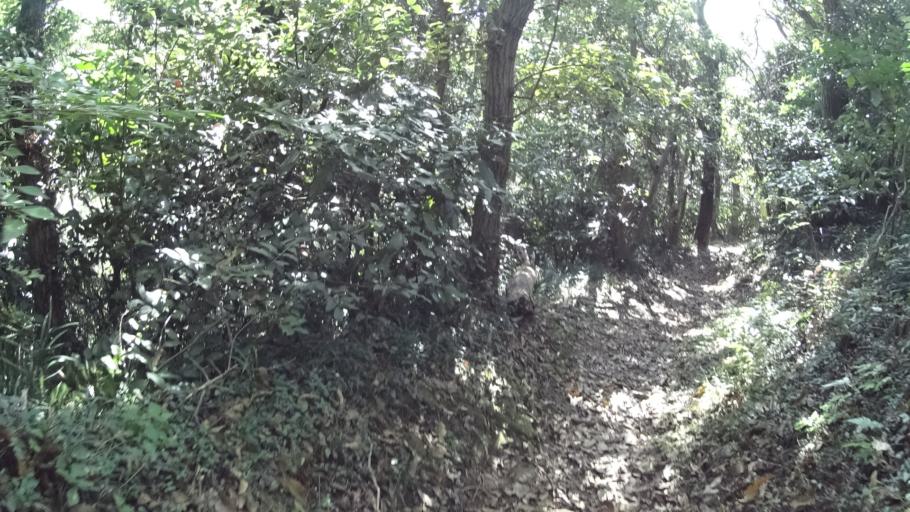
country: JP
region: Kanagawa
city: Yokosuka
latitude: 35.2771
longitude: 139.6239
